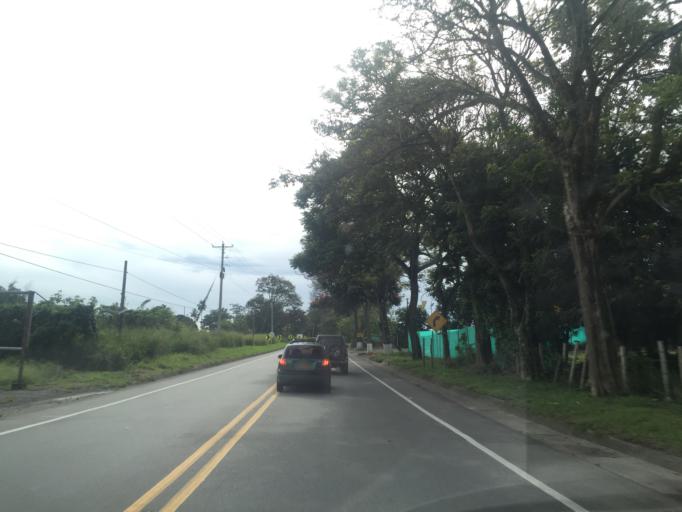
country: CO
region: Quindio
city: La Tebaida
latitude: 4.4615
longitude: -75.7832
